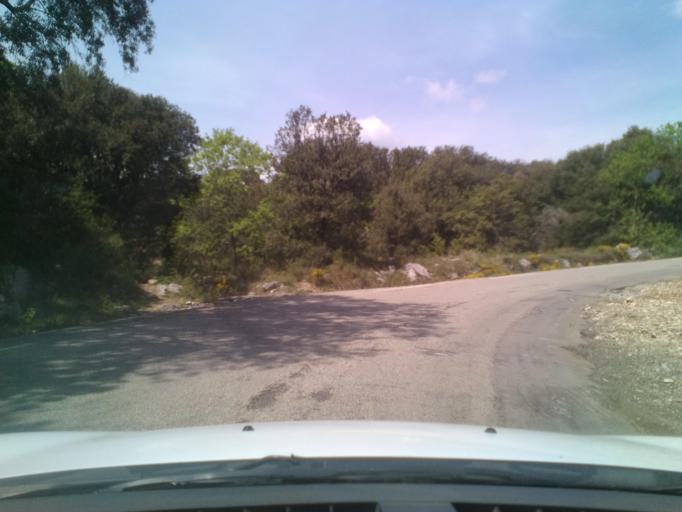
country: FR
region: Languedoc-Roussillon
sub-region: Departement du Gard
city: Saint-Hippolyte-du-Fort
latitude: 43.9736
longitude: 3.8819
